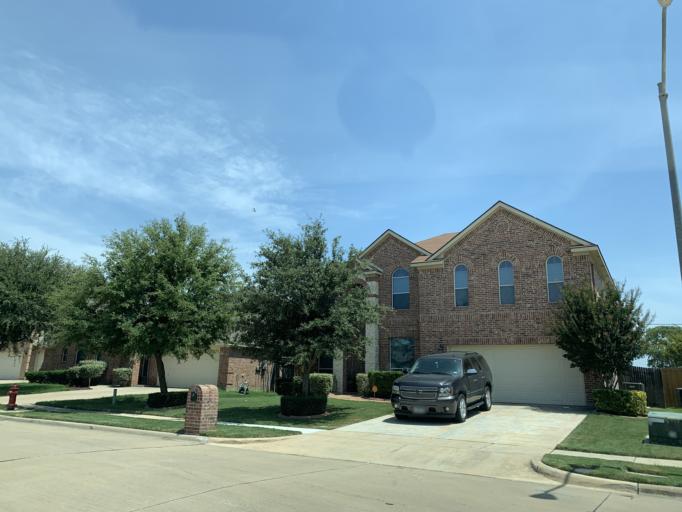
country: US
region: Texas
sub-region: Dallas County
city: Grand Prairie
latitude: 32.6519
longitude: -97.0357
